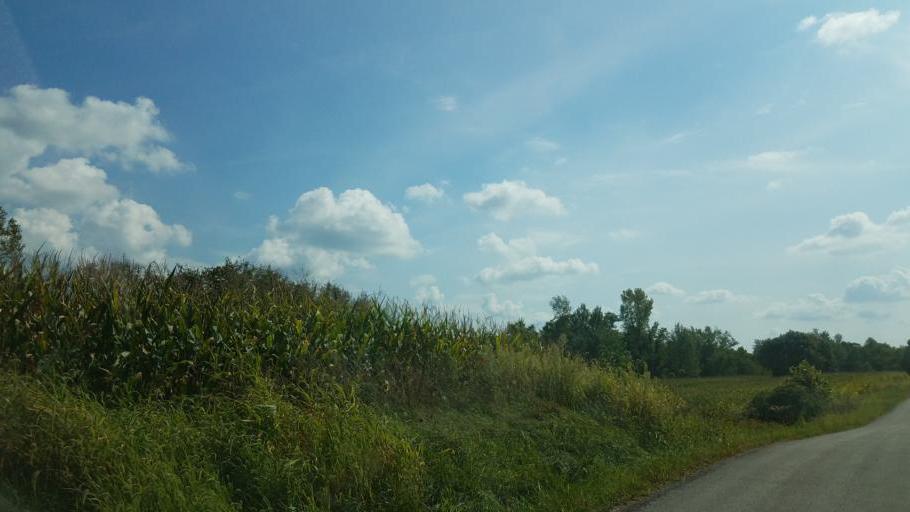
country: US
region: Ohio
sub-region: Knox County
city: Centerburg
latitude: 40.3610
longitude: -82.6351
